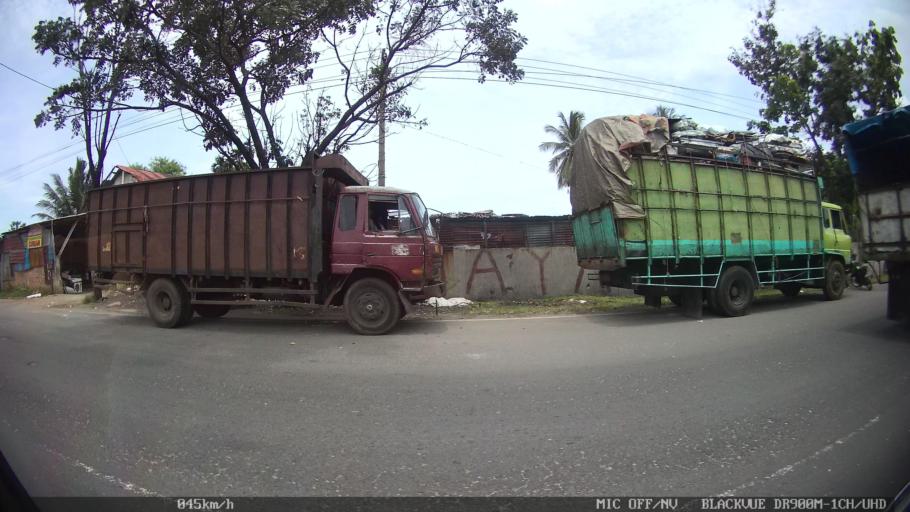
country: ID
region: North Sumatra
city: Sunggal
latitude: 3.5229
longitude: 98.6192
